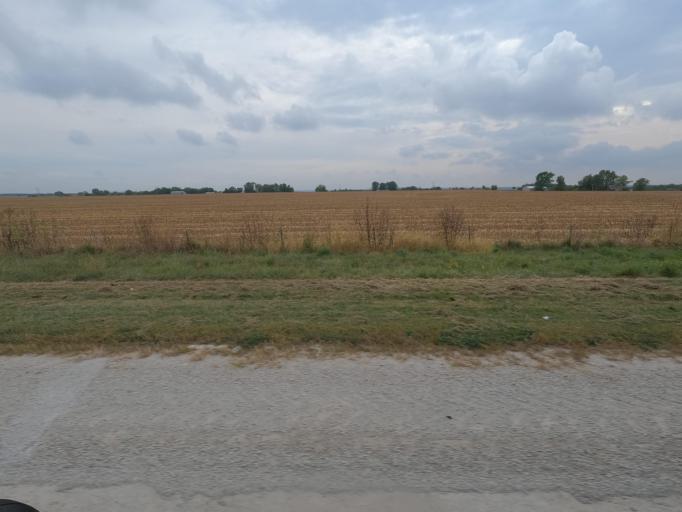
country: US
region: Iowa
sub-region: Wapello County
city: Ottumwa
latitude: 41.0961
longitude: -92.4590
